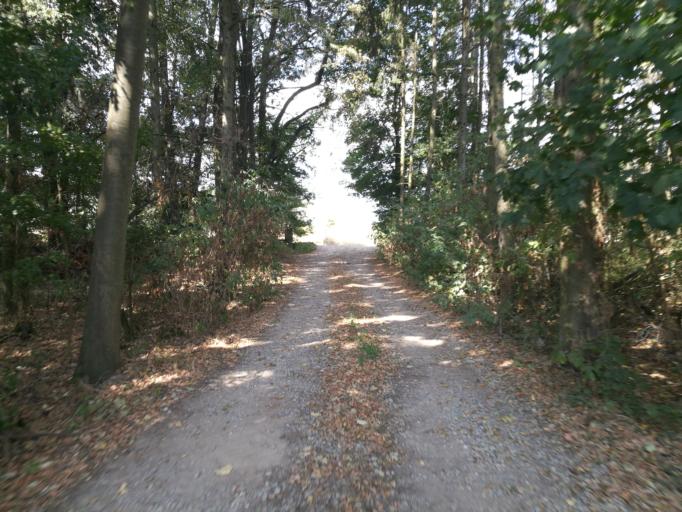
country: DE
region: Bavaria
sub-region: Regierungsbezirk Mittelfranken
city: Seukendorf
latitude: 49.4952
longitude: 10.9003
